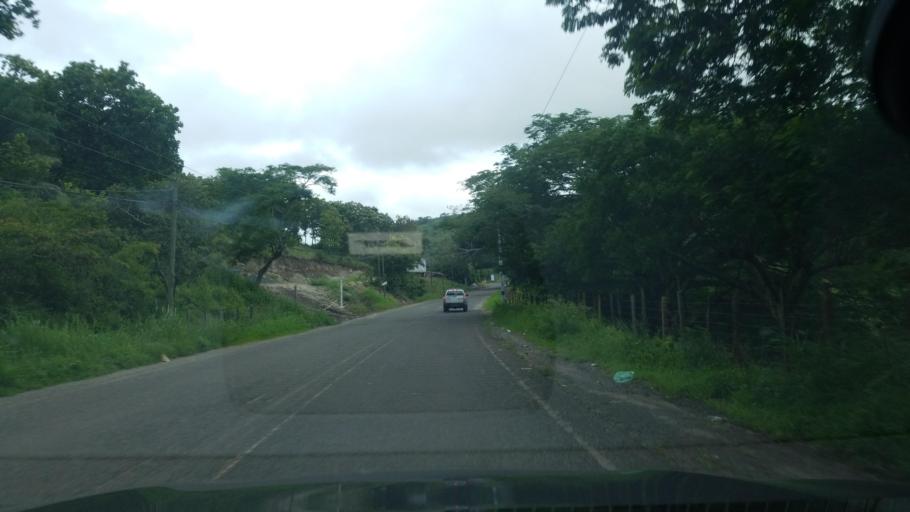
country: HN
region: Choluteca
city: San Marcos de Colon
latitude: 13.4344
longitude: -86.8235
